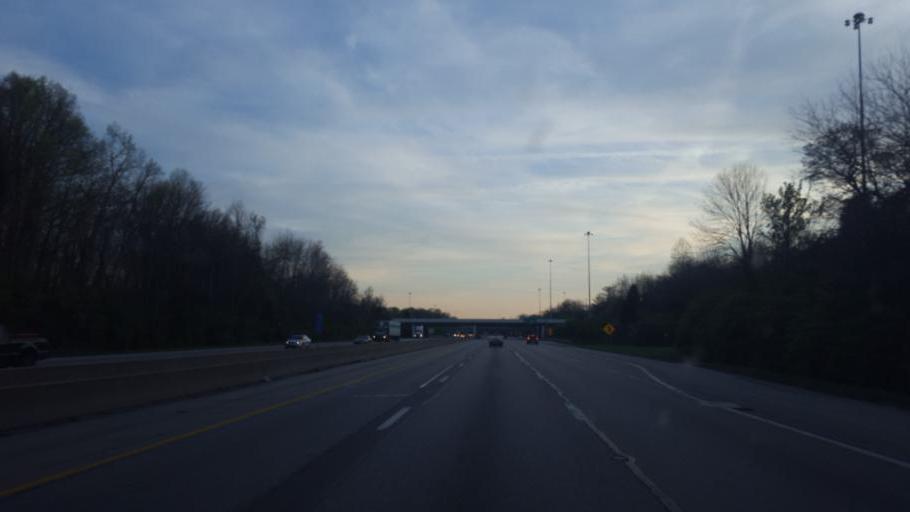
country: US
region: Ohio
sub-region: Hamilton County
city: Highpoint
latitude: 39.2727
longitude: -84.3490
